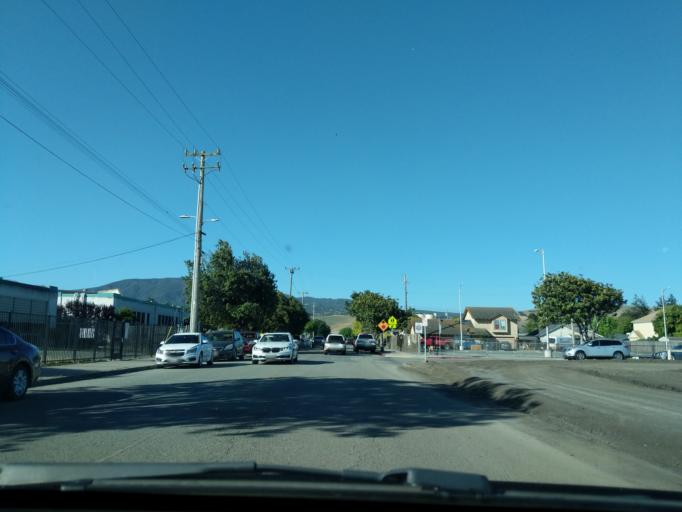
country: US
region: California
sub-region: Monterey County
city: Salinas
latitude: 36.6266
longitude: -121.6448
